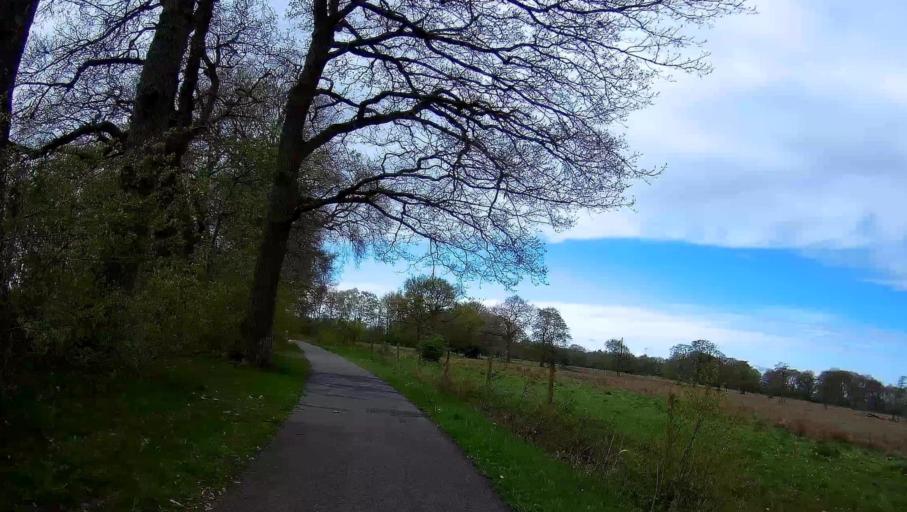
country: NL
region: Drenthe
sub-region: Gemeente Aa en Hunze
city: Anloo
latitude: 52.9635
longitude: 6.7078
